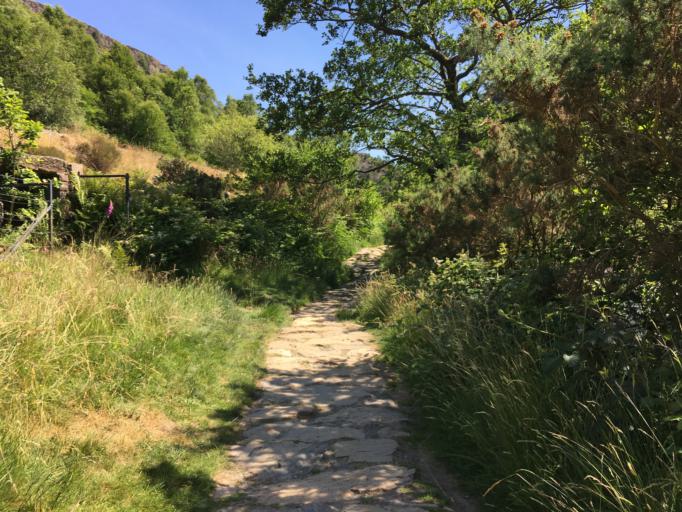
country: GB
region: Wales
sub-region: Gwynedd
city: Penrhyndeudraeth
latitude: 53.0014
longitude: -4.0986
